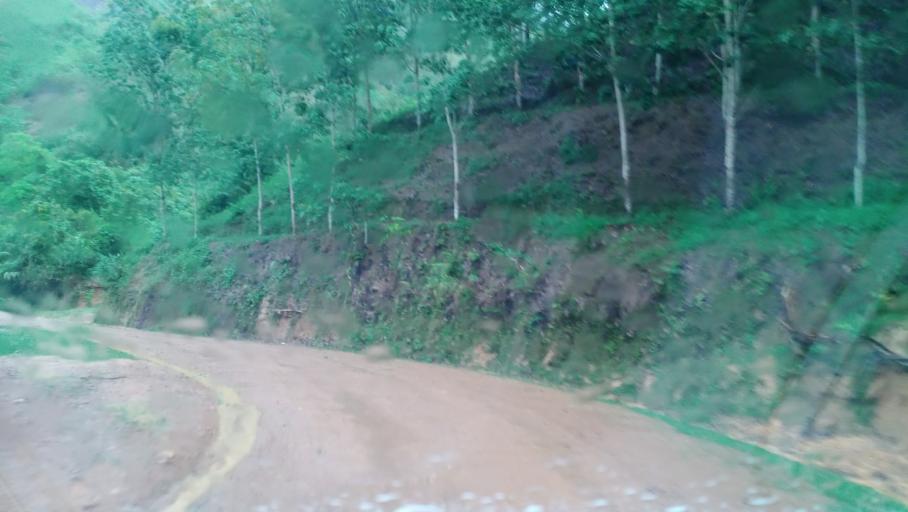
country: LA
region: Phongsali
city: Khoa
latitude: 21.1302
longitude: 102.3223
